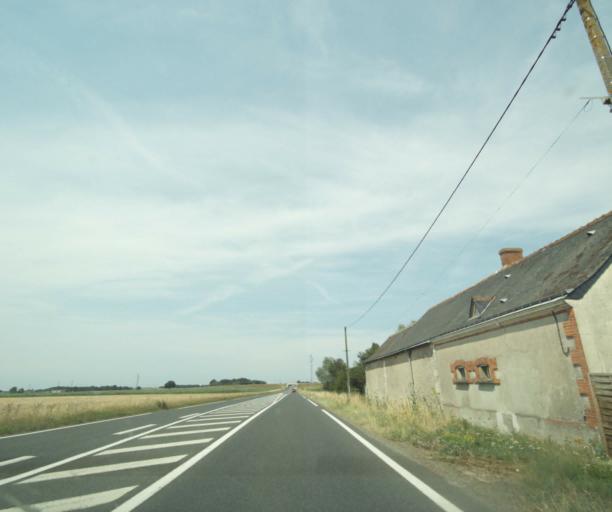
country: FR
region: Centre
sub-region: Departement d'Indre-et-Loire
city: Sainte-Maure-de-Touraine
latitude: 47.1746
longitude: 0.6560
